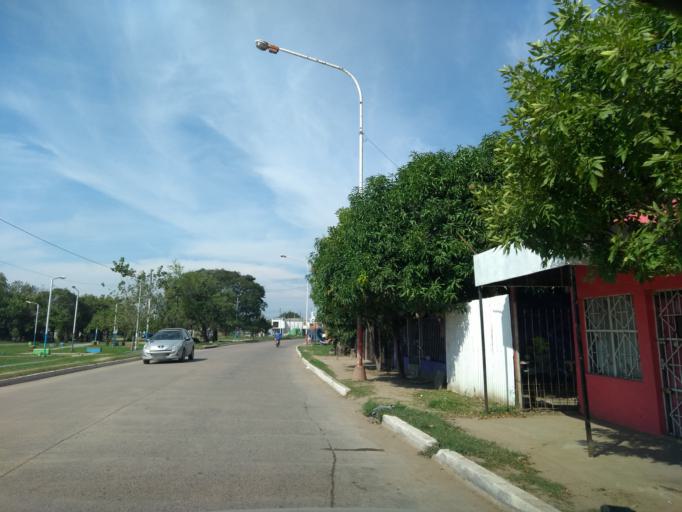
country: AR
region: Chaco
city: Barranqueras
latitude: -27.4639
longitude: -58.9512
